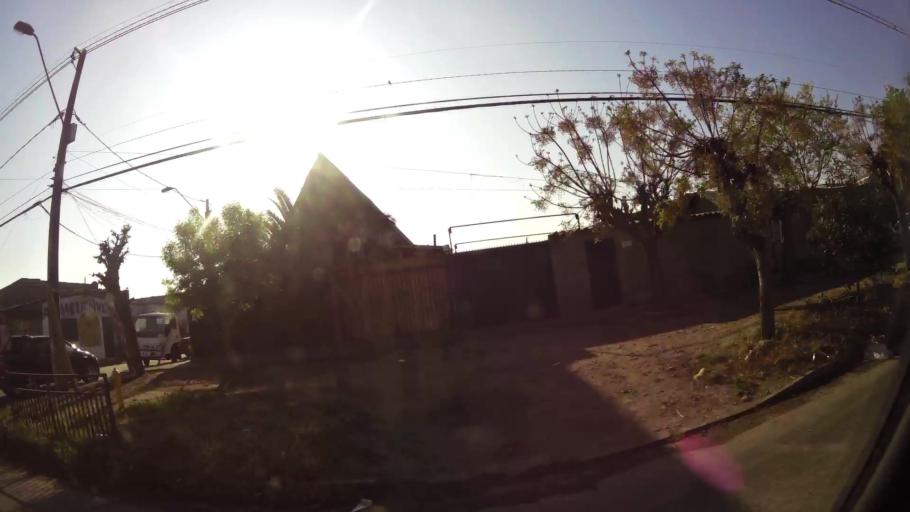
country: CL
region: Santiago Metropolitan
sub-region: Provincia de Santiago
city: Santiago
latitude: -33.4929
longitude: -70.6312
